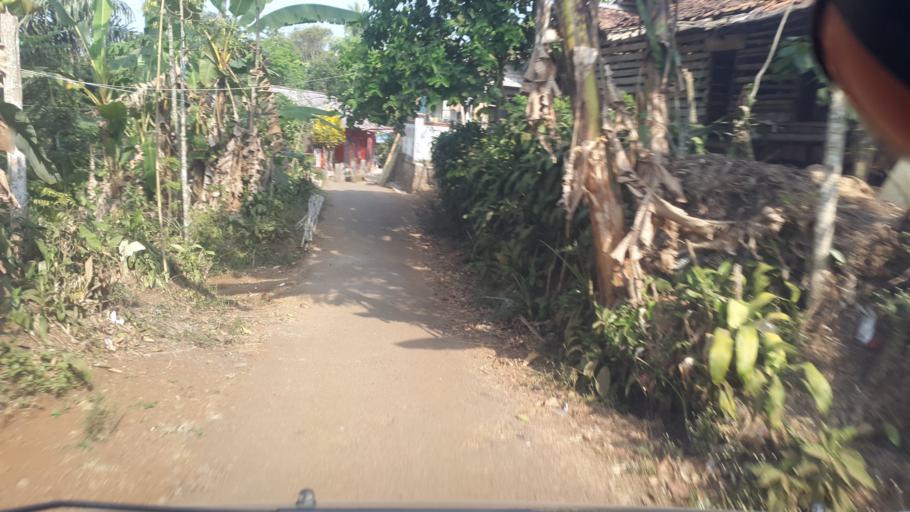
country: ID
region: West Java
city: Cipari Satu
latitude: -7.1120
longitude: 106.8593
